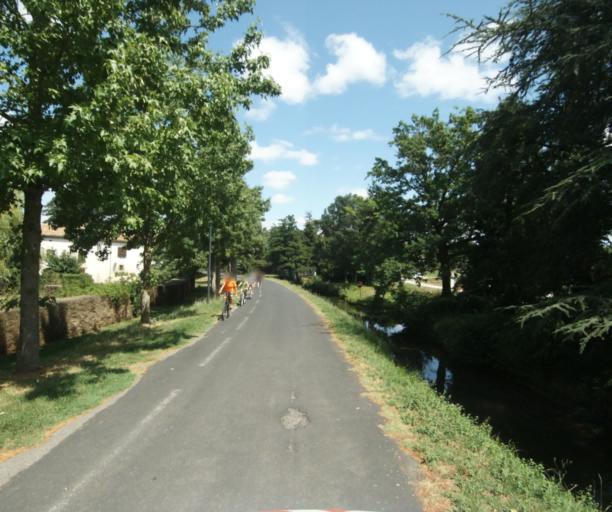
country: FR
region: Midi-Pyrenees
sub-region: Departement de la Haute-Garonne
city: Revel
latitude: 43.4538
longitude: 2.0134
